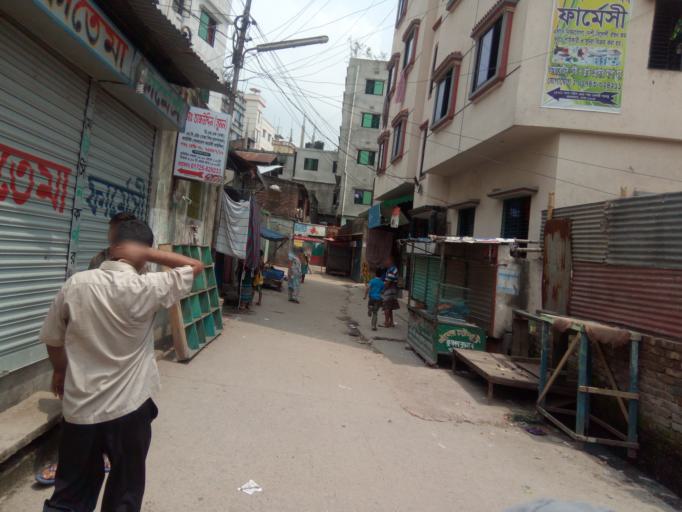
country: BD
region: Dhaka
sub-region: Dhaka
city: Dhaka
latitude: 23.6883
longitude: 90.4370
